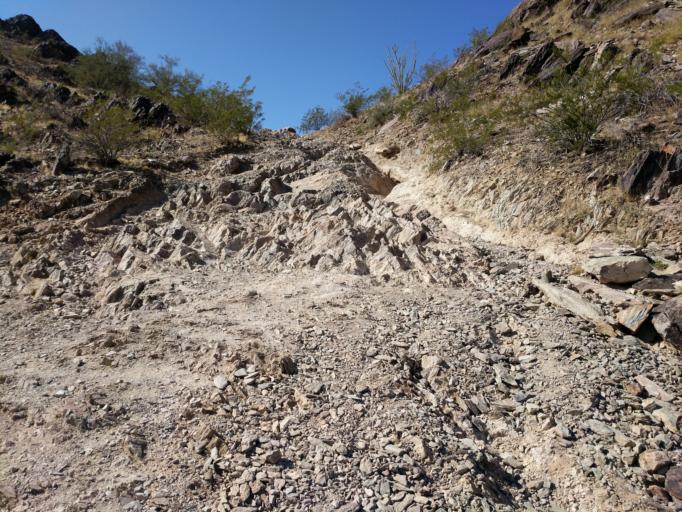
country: US
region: Arizona
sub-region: Maricopa County
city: Glendale
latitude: 33.5886
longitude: -112.0822
